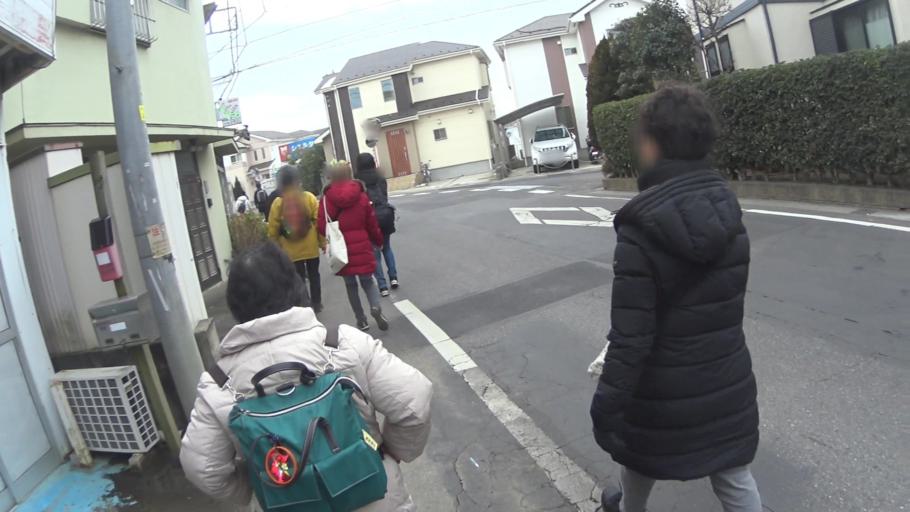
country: JP
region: Chiba
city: Funabashi
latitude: 35.7498
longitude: 139.9909
